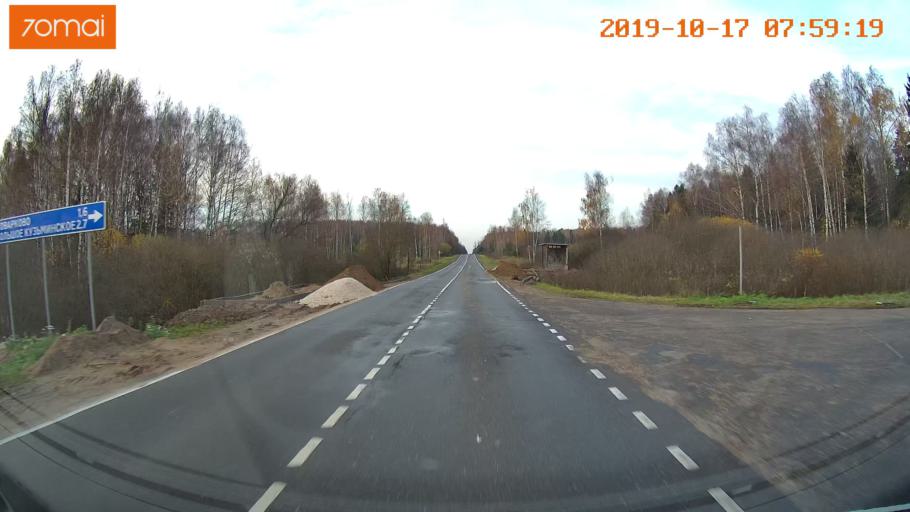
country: RU
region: Vladimir
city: Bavleny
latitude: 56.3945
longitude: 39.5408
